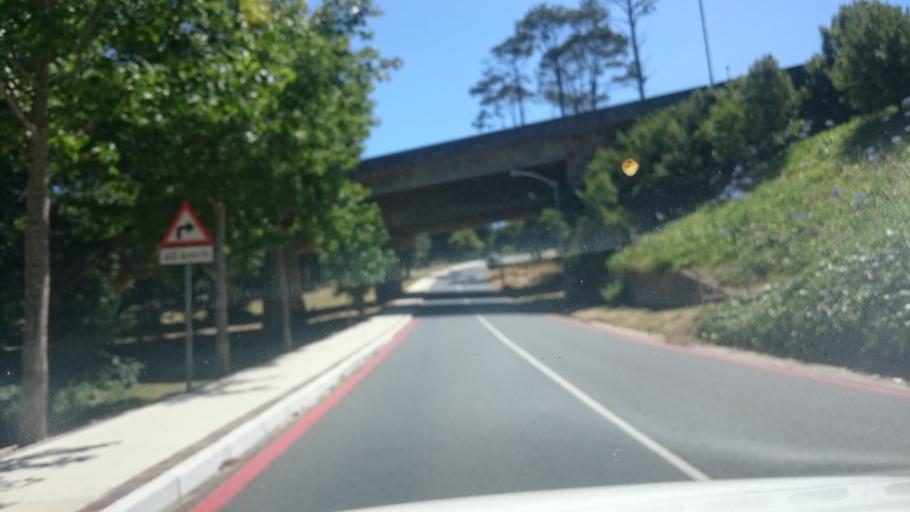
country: ZA
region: Western Cape
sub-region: City of Cape Town
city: Newlands
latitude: -33.9999
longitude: 18.4506
